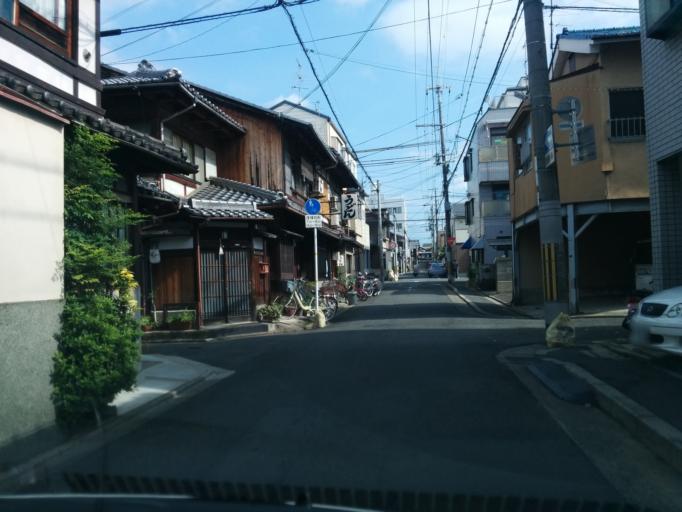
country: JP
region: Kyoto
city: Muko
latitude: 34.9878
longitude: 135.7346
